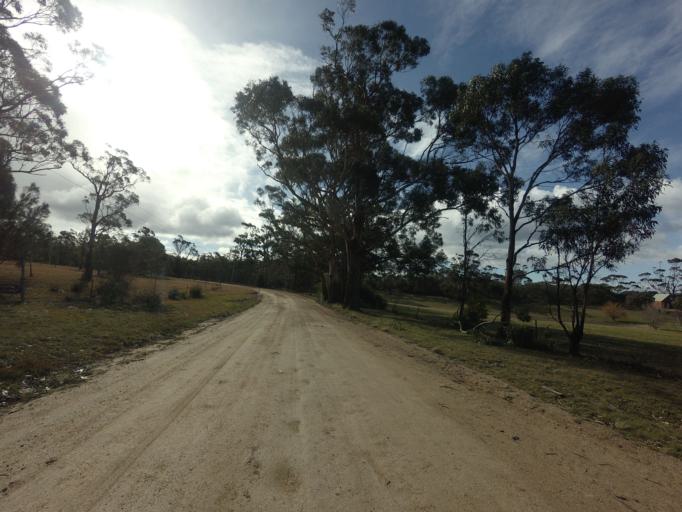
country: AU
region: Tasmania
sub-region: Sorell
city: Sorell
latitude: -42.3042
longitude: 147.9964
